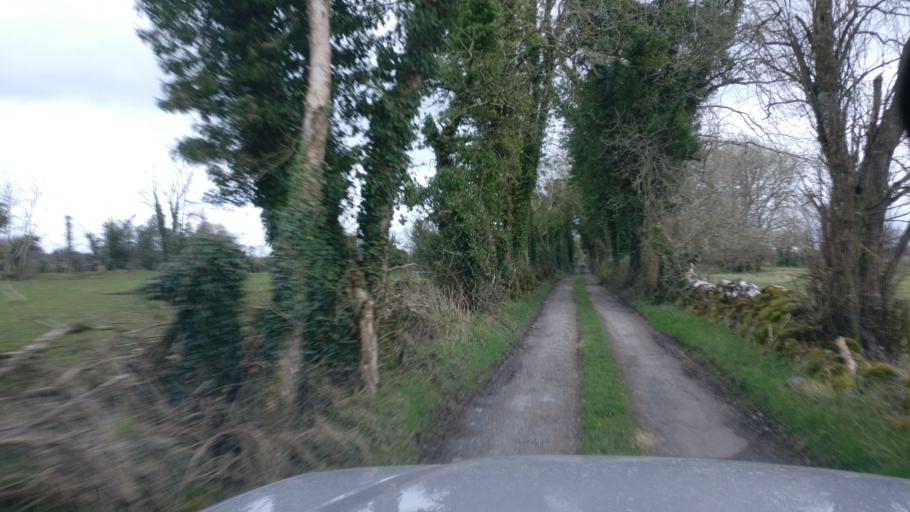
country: IE
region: Connaught
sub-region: County Galway
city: Loughrea
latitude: 53.2537
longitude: -8.4583
